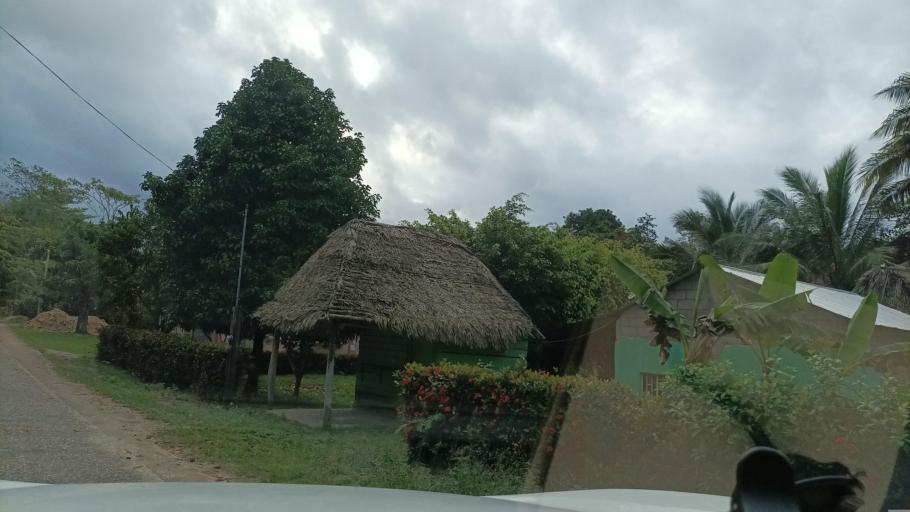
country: MX
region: Veracruz
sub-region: Moloacan
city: Cuichapa
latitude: 17.9215
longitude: -94.3684
